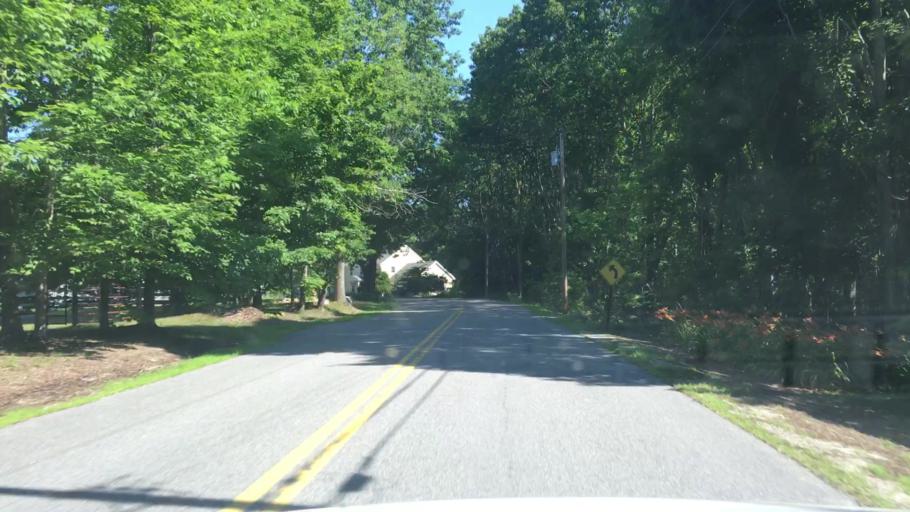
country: US
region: Maine
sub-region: Cumberland County
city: Cumberland Center
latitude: 43.7941
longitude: -70.3214
